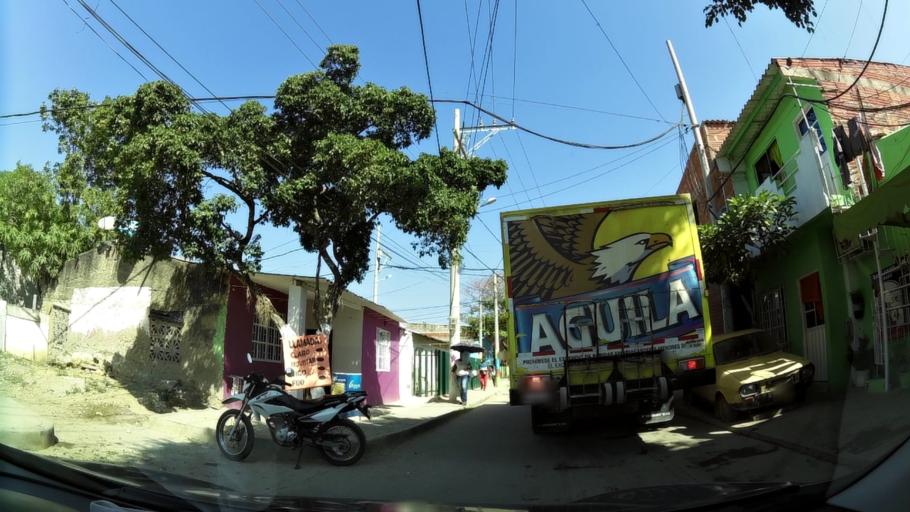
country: CO
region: Bolivar
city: Cartagena
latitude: 10.3723
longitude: -75.4971
